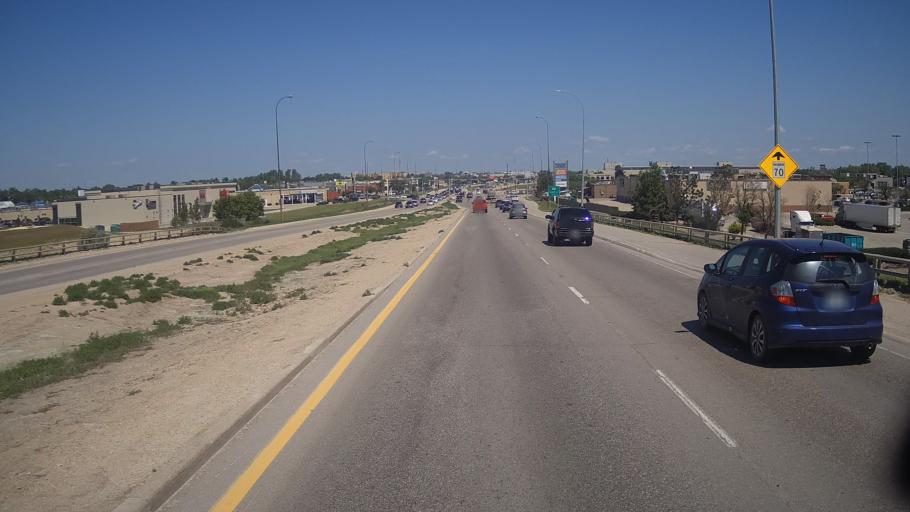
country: CA
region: Manitoba
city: Winnipeg
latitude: 49.8951
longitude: -97.0704
